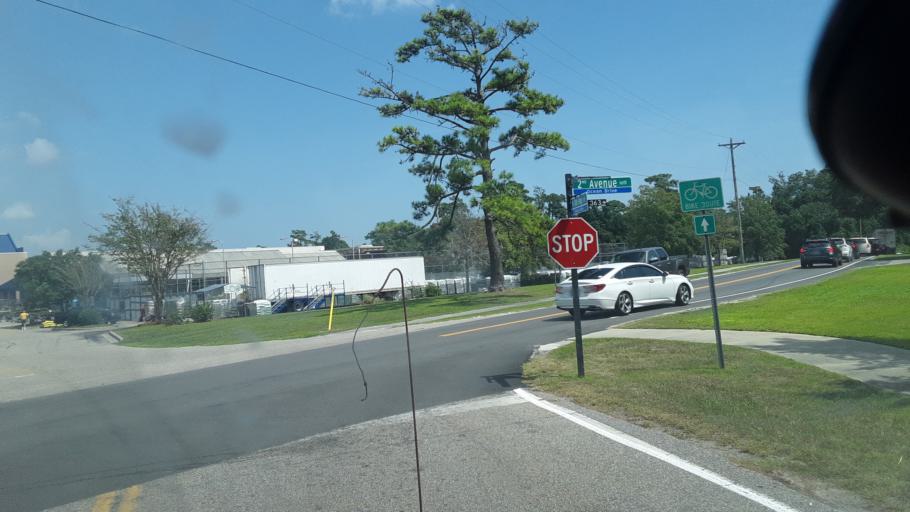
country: US
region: South Carolina
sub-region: Horry County
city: North Myrtle Beach
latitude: 33.8284
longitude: -78.6767
